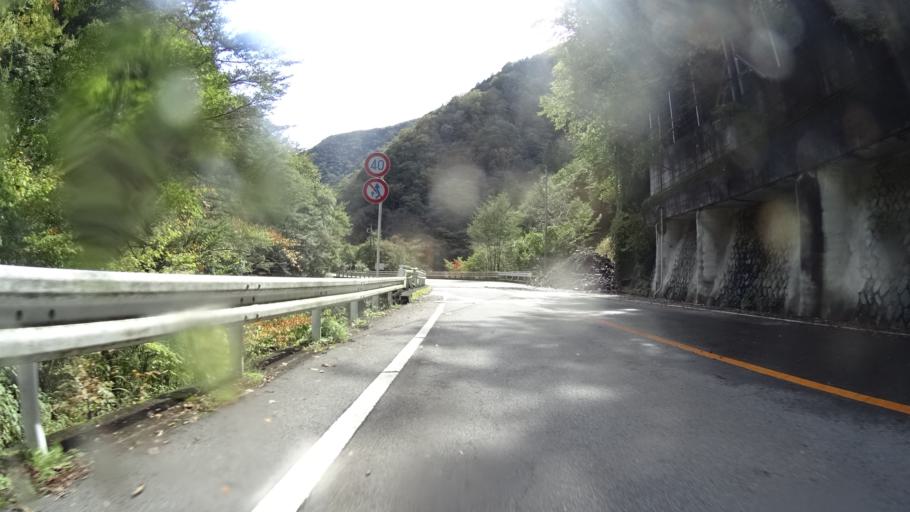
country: JP
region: Yamanashi
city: Enzan
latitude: 35.7975
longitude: 138.8958
